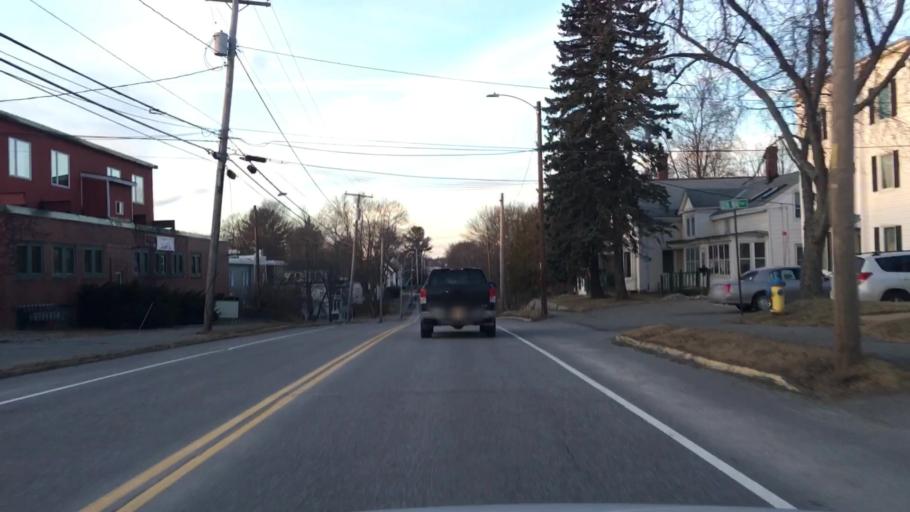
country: US
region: Maine
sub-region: Penobscot County
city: Brewer
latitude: 44.7911
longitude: -68.7569
